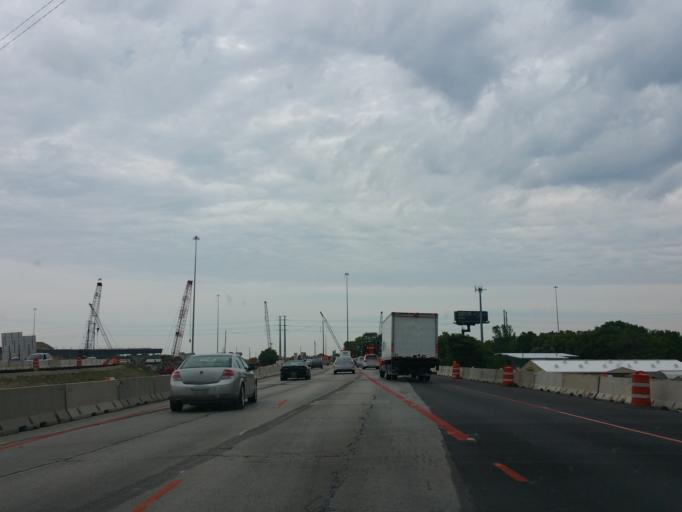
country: US
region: Wisconsin
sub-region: Milwaukee County
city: West Allis
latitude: 43.0269
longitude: -88.0412
